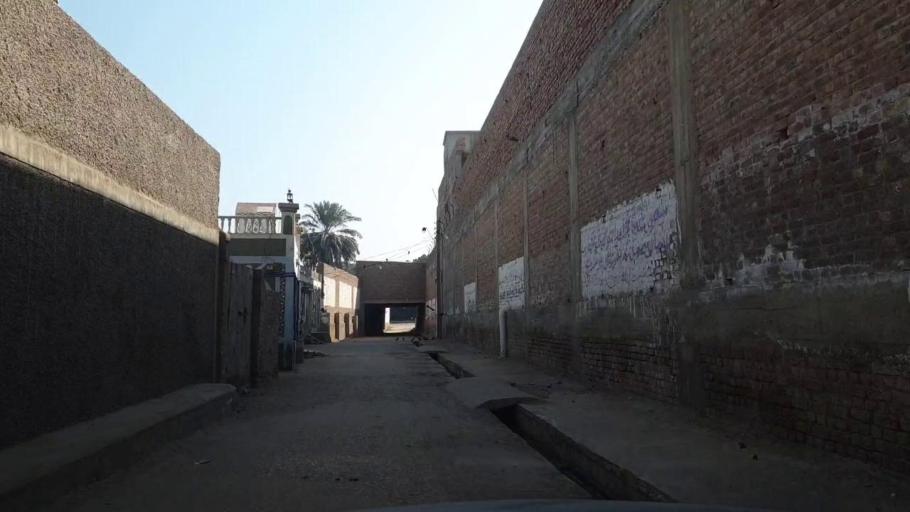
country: PK
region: Sindh
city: Tando Allahyar
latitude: 25.5158
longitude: 68.7109
